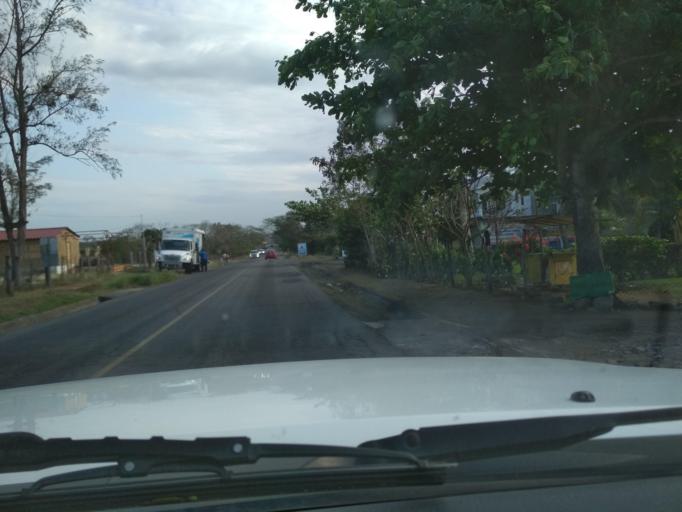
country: MX
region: Veracruz
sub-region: Veracruz
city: Delfino Victoria (Santa Fe)
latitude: 19.1497
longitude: -96.2991
